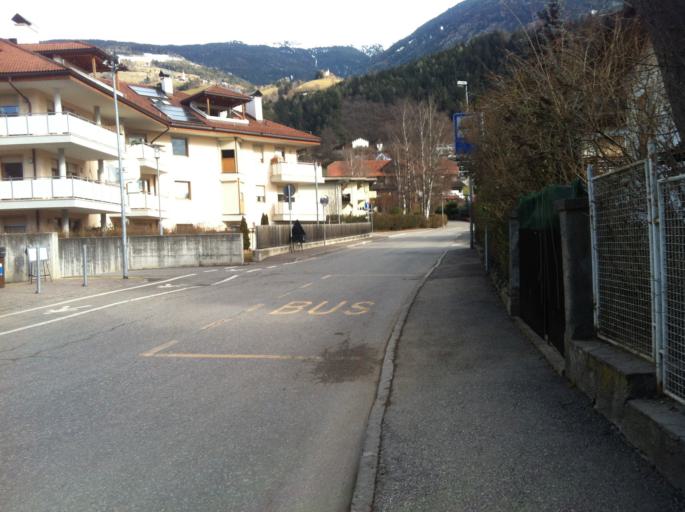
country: IT
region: Trentino-Alto Adige
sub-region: Bolzano
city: Bressanone
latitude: 46.7139
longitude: 11.6630
